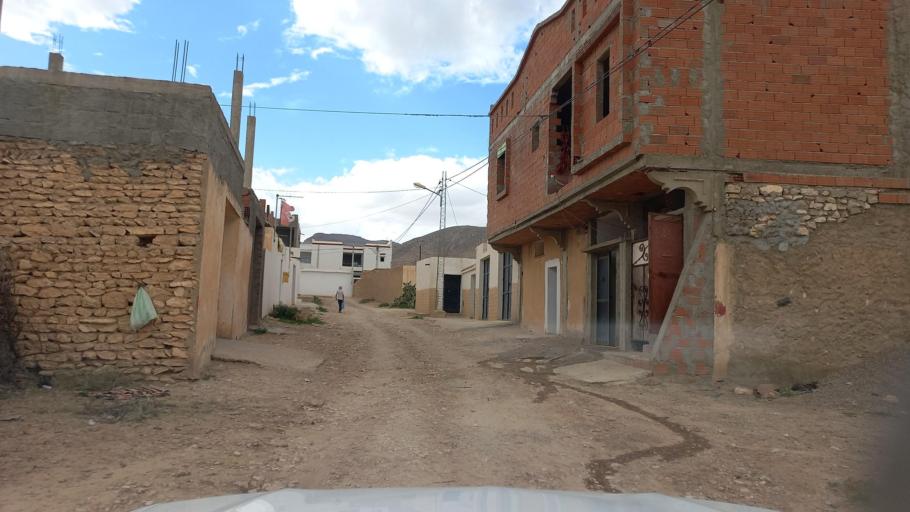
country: TN
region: Al Qasrayn
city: Sbiba
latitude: 35.4467
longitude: 9.0784
